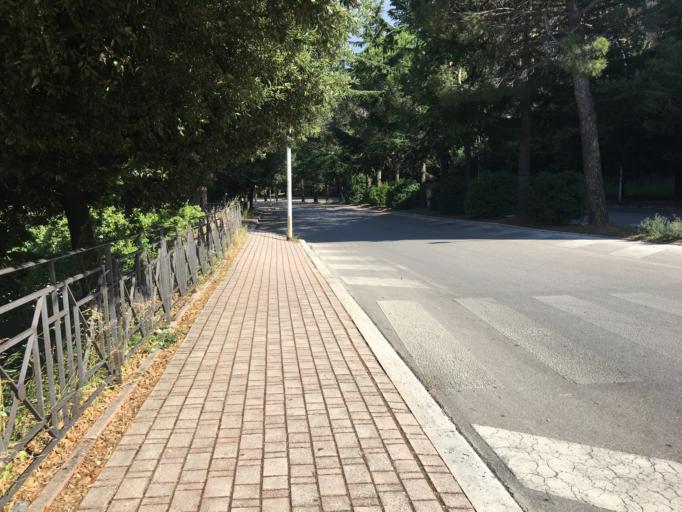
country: IT
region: Molise
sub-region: Provincia di Campobasso
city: Campobasso
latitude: 41.5540
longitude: 14.6621
